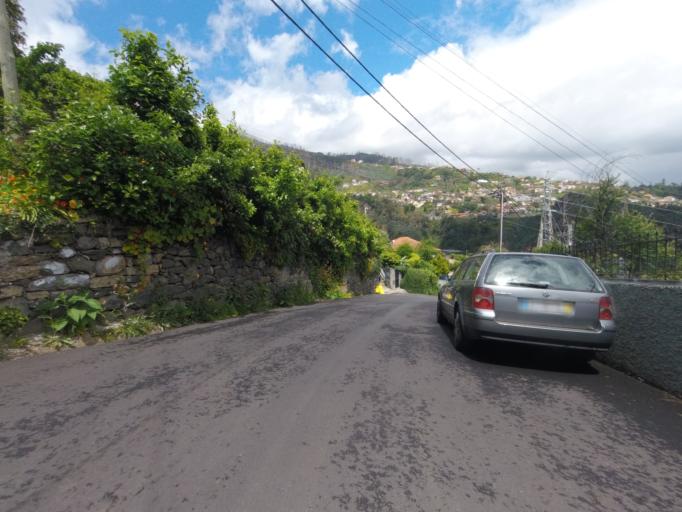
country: PT
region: Madeira
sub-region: Funchal
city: Nossa Senhora do Monte
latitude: 32.6790
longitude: -16.9206
